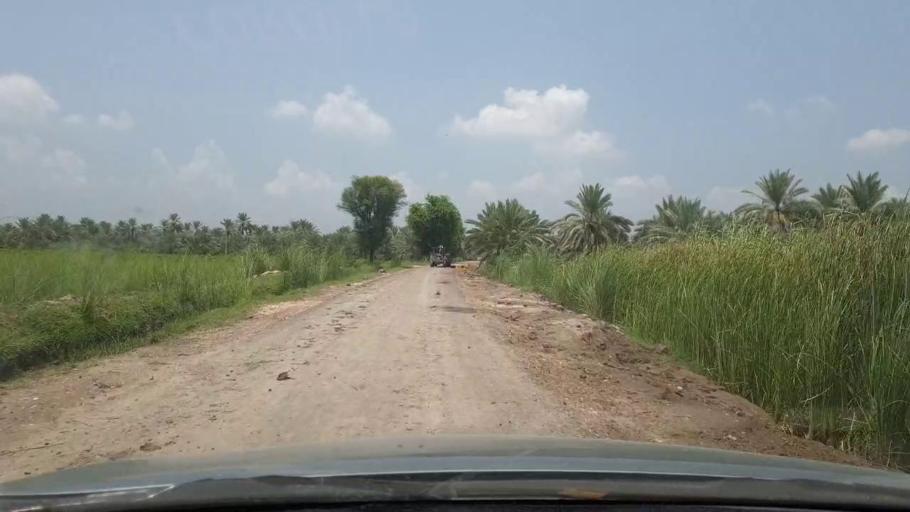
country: PK
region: Sindh
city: Khairpur
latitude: 27.4683
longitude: 68.7366
